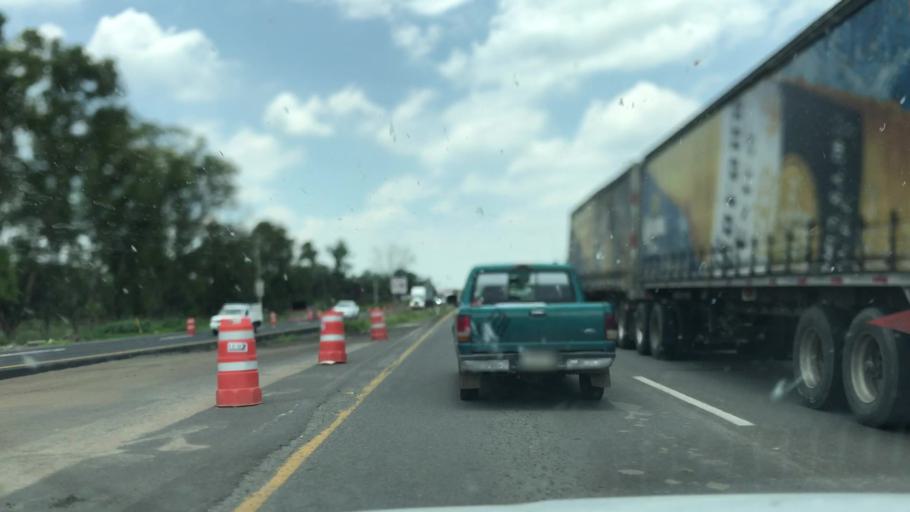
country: MX
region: Guanajuato
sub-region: Irapuato
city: San Ignacio de Rivera (Ojo de Agua)
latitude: 20.5344
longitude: -101.4589
